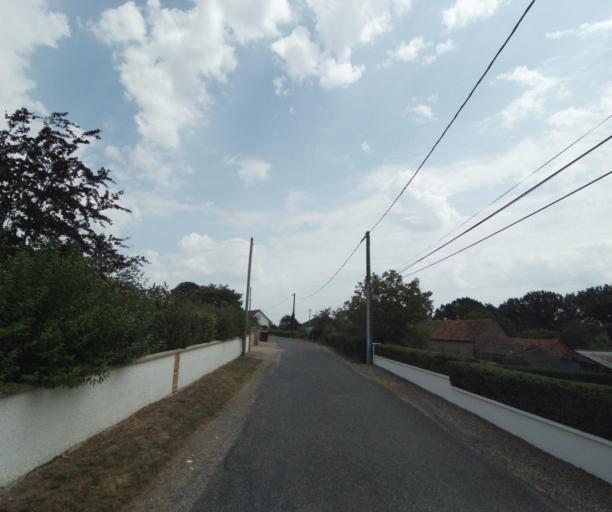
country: FR
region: Bourgogne
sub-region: Departement de Saone-et-Loire
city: Gueugnon
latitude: 46.6013
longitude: 4.0157
